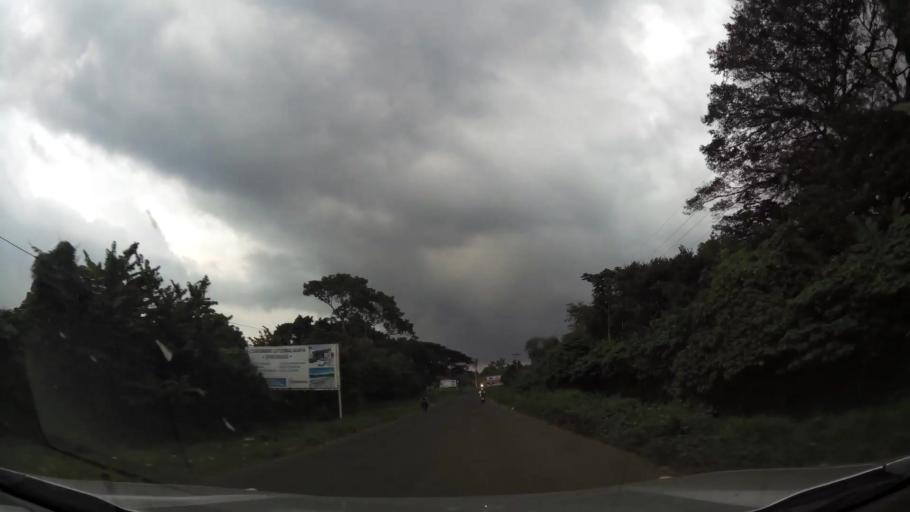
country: GT
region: Escuintla
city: Santa Lucia Cotzumalguapa
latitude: 14.3232
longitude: -91.0356
